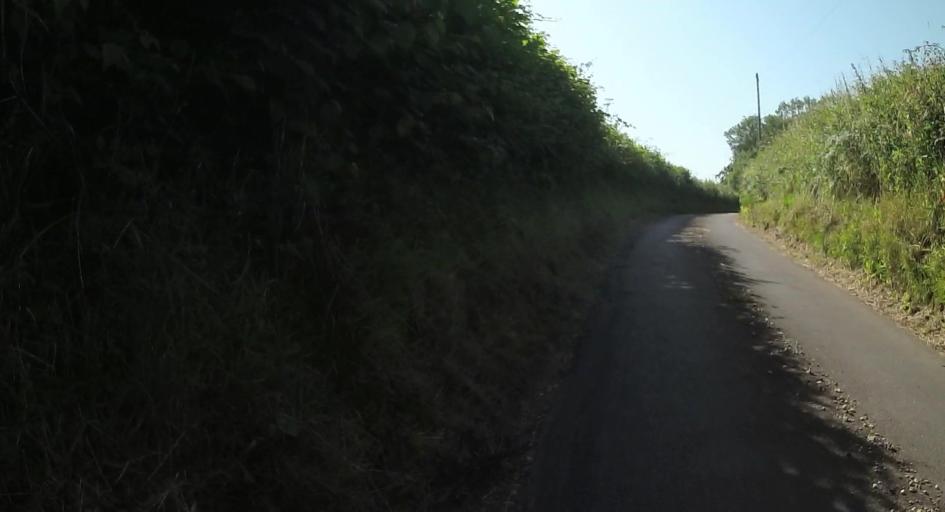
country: GB
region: England
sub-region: Hampshire
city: Long Sutton
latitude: 51.1829
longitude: -0.9294
